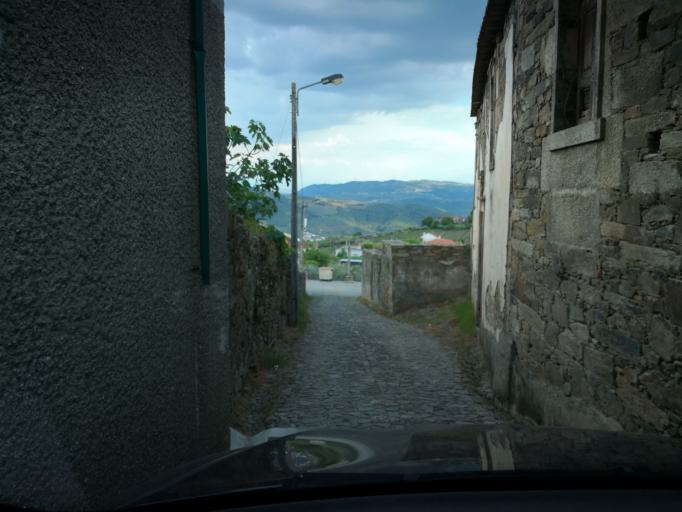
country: PT
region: Vila Real
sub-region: Sabrosa
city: Vilela
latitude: 41.2086
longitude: -7.6599
